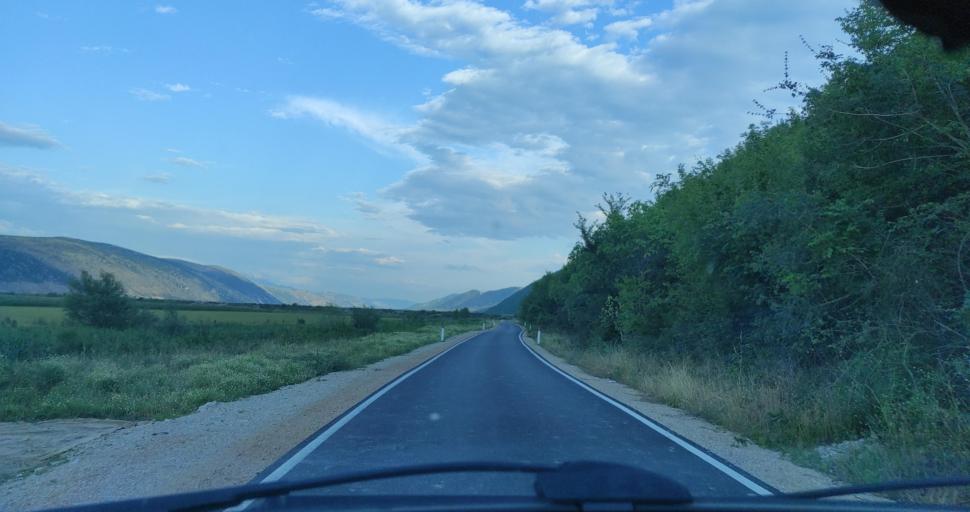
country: AL
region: Shkoder
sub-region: Rrethi i Shkodres
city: Velipoje
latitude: 41.9259
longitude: 19.4488
